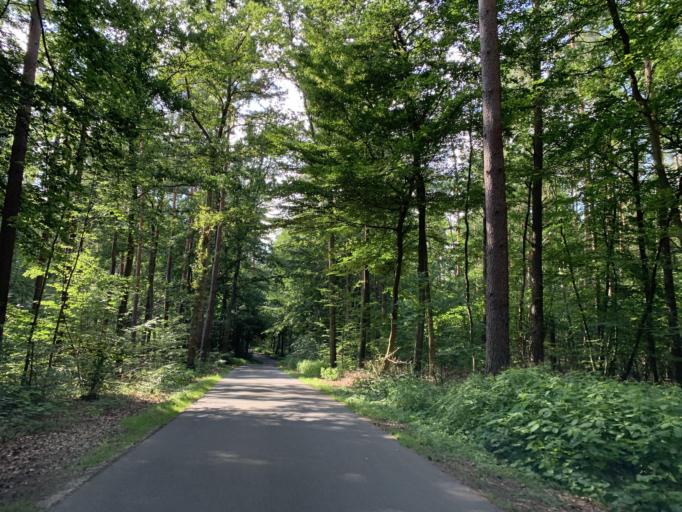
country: DE
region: Mecklenburg-Vorpommern
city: Carpin
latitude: 53.3833
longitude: 13.2149
